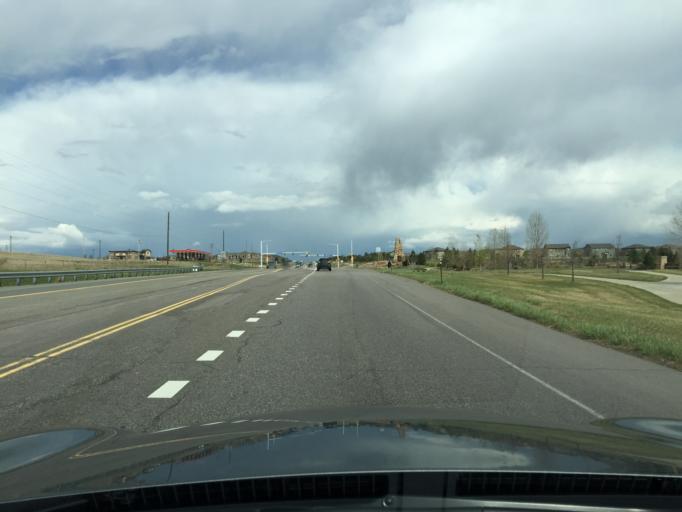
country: US
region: Colorado
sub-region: Boulder County
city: Lafayette
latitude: 40.0002
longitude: -105.0404
